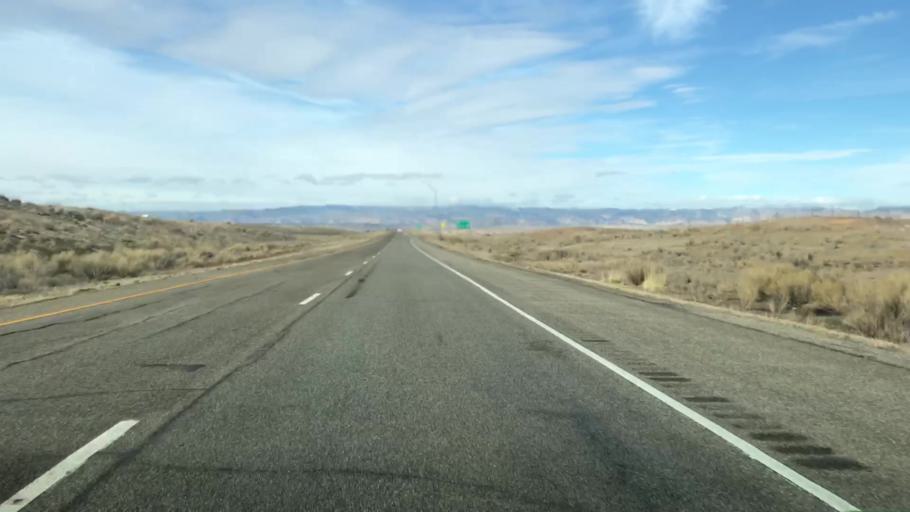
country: US
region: Colorado
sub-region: Mesa County
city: Loma
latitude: 39.2103
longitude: -108.8627
